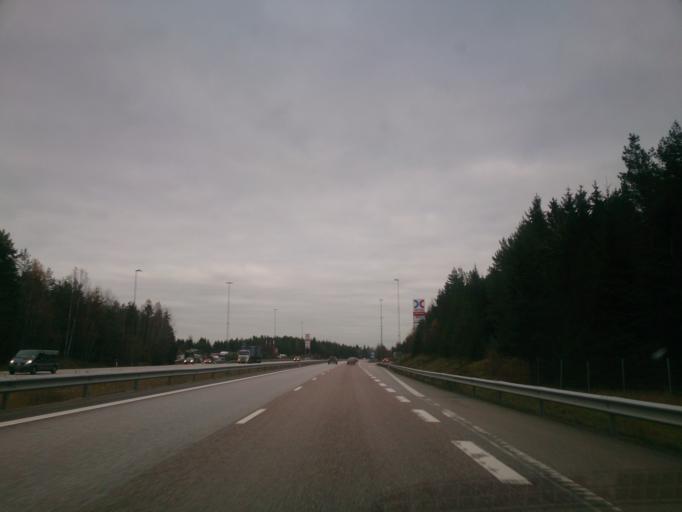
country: SE
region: Soedermanland
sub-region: Gnesta Kommun
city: Gnesta
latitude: 58.9159
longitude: 17.3637
